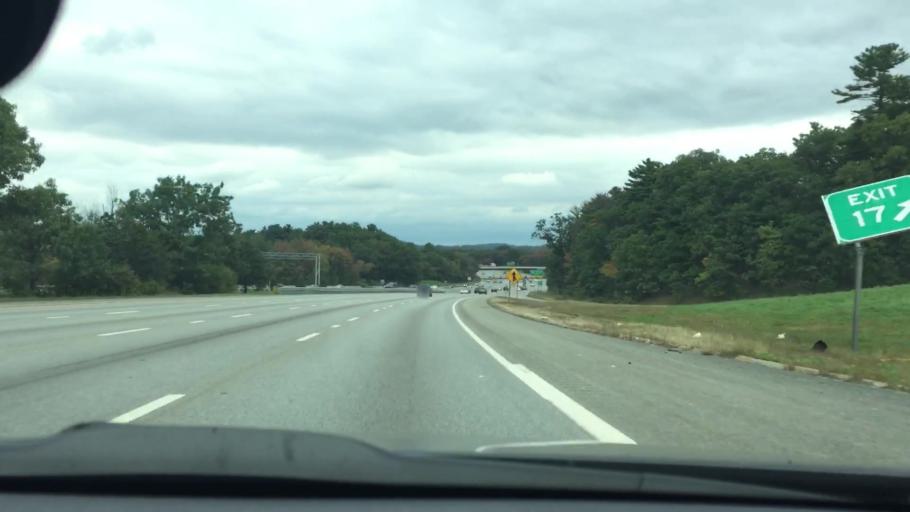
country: US
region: Massachusetts
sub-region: Norfolk County
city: Needham
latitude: 42.2649
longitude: -71.2048
